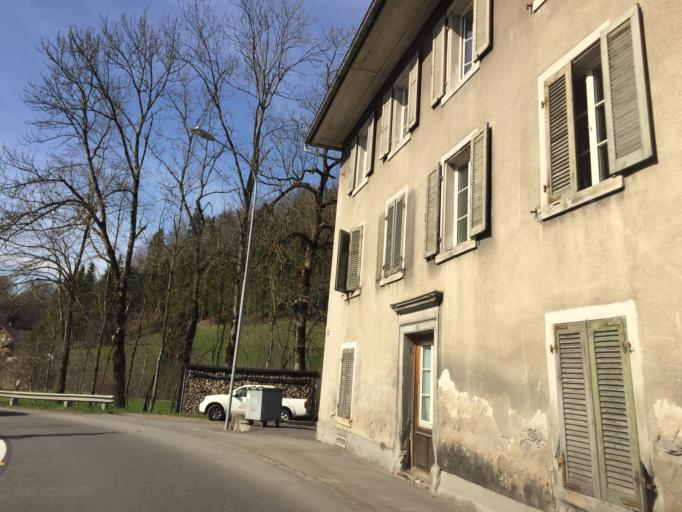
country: CH
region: Zug
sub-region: Zug
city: Unterageri
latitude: 47.1534
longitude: 8.5626
